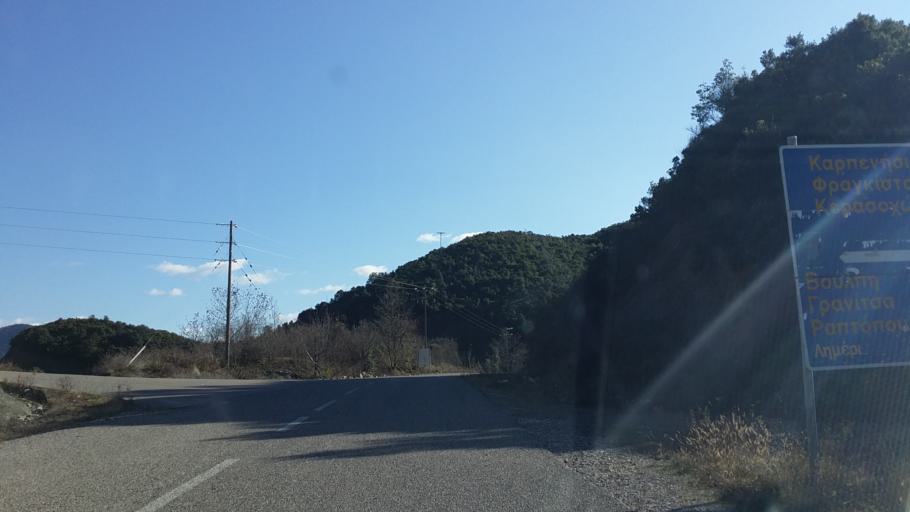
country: GR
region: Central Greece
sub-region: Nomos Evrytanias
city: Kerasochori
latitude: 39.0050
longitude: 21.5364
